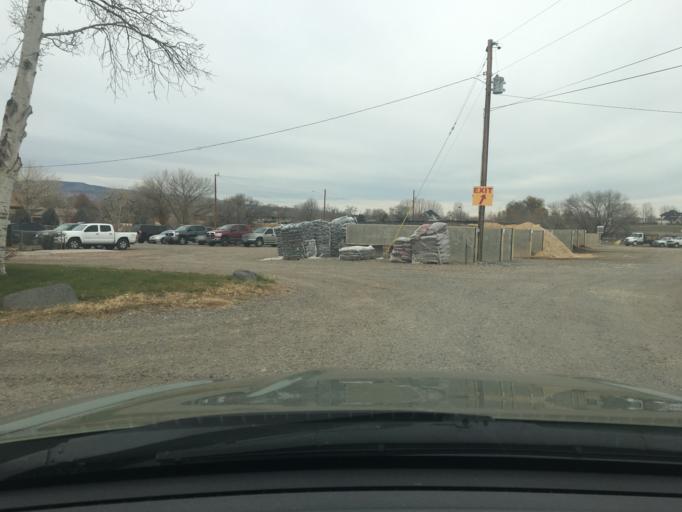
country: US
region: Colorado
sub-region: Mesa County
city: Grand Junction
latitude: 39.1136
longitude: -108.5724
